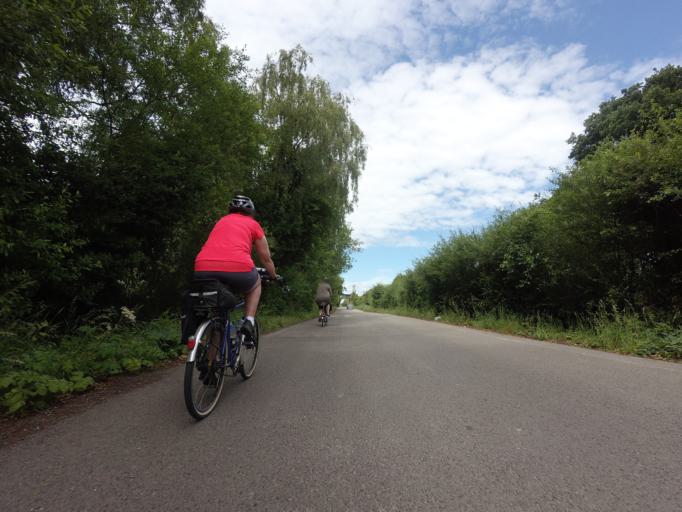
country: GB
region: England
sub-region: Kent
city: Cliffe
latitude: 51.4377
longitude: 0.4542
